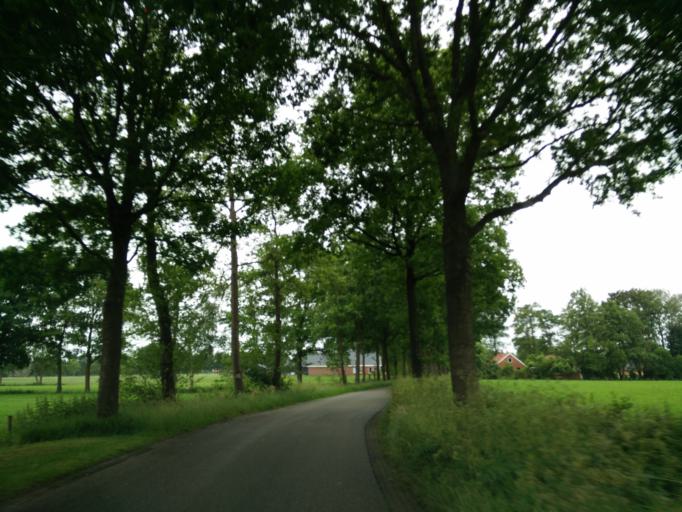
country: NL
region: Groningen
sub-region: Gemeente Leek
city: Leek
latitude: 53.1428
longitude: 6.4755
